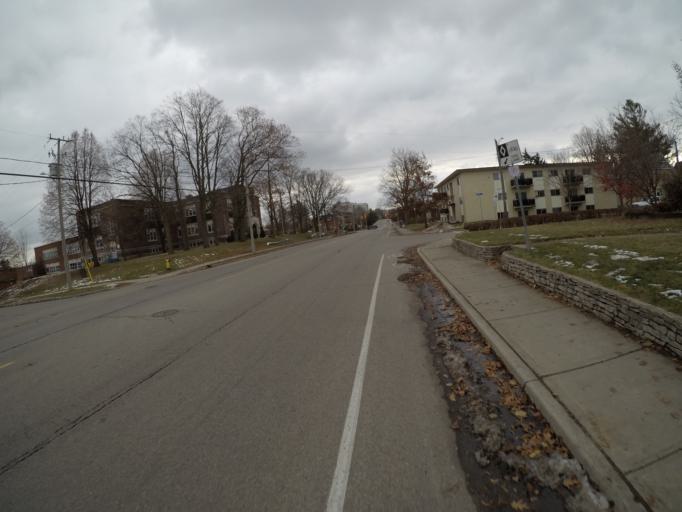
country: CA
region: Ontario
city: Waterloo
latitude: 43.4596
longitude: -80.4911
